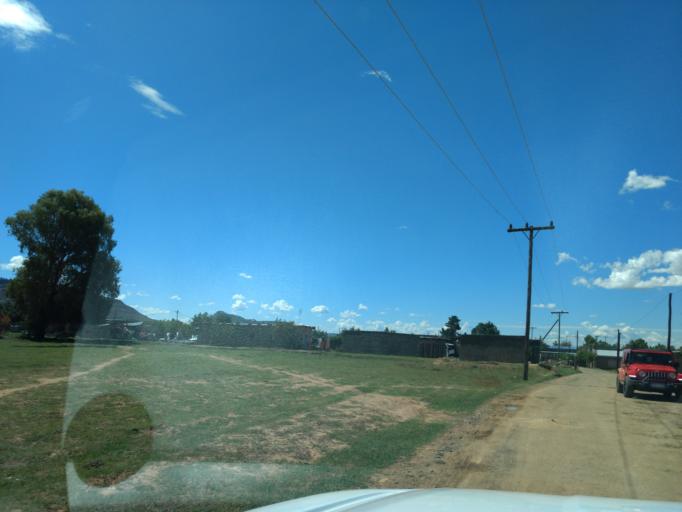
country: LS
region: Maseru
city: Maseru
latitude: -29.3718
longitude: 27.5111
